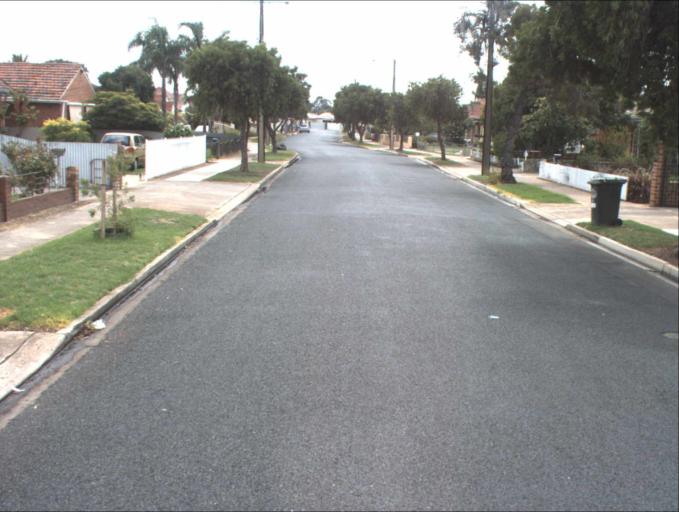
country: AU
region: South Australia
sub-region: Charles Sturt
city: Woodville
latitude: -34.8808
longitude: 138.5600
